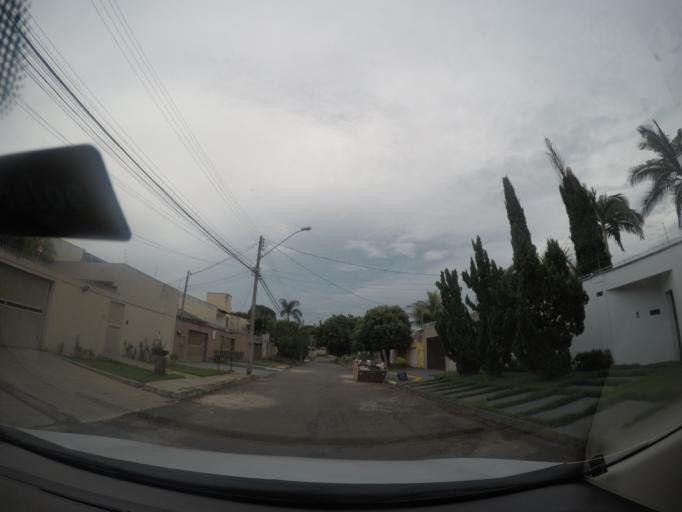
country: BR
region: Goias
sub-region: Goiania
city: Goiania
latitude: -16.6475
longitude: -49.2257
